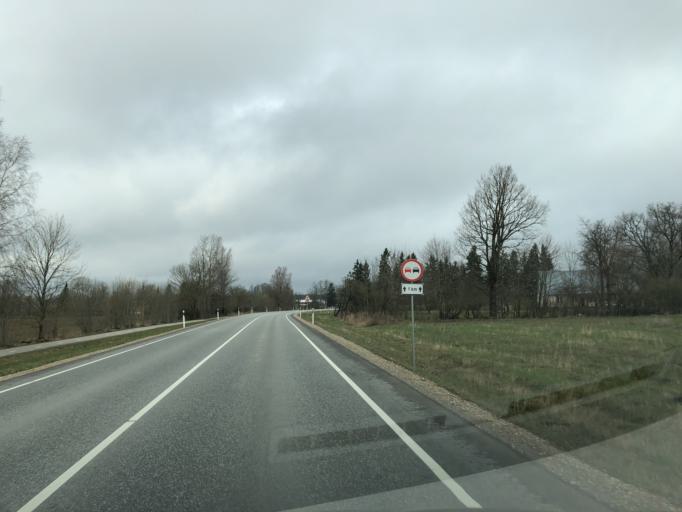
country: EE
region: Jogevamaa
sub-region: Jogeva linn
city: Jogeva
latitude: 58.7545
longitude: 26.3401
